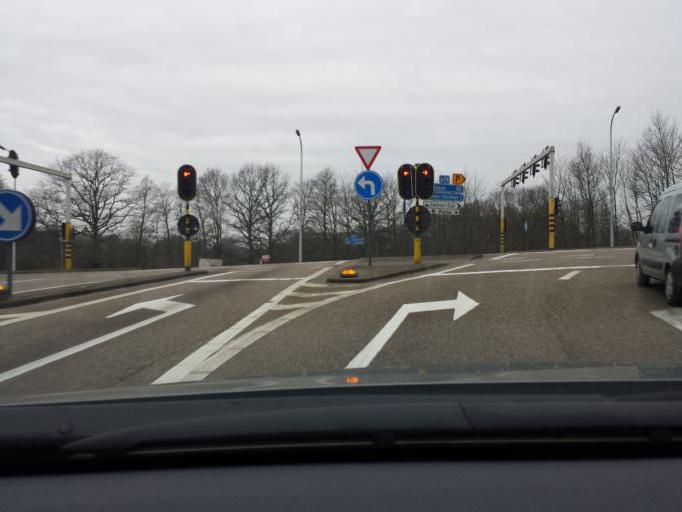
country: BE
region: Flanders
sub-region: Provincie Limburg
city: Zonhoven
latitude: 51.0105
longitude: 5.3718
